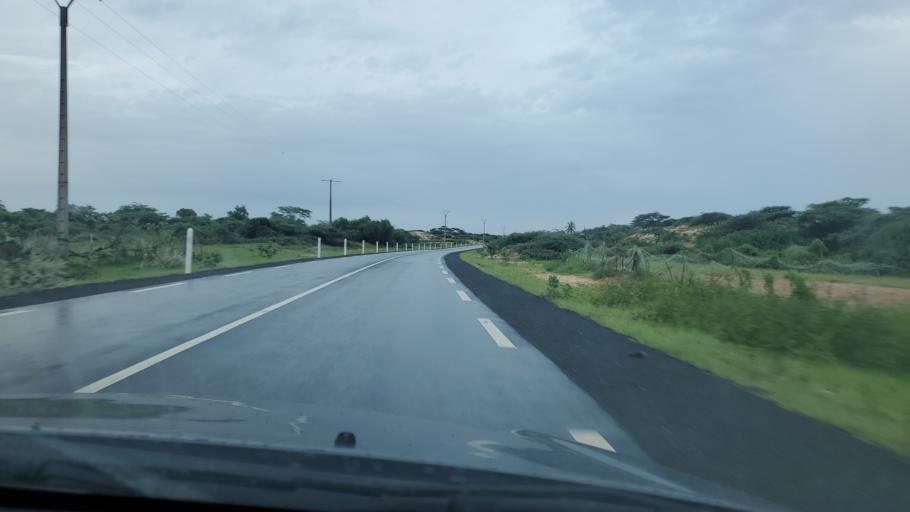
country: SN
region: Saint-Louis
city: Saint-Louis
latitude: 15.8143
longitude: -16.5181
